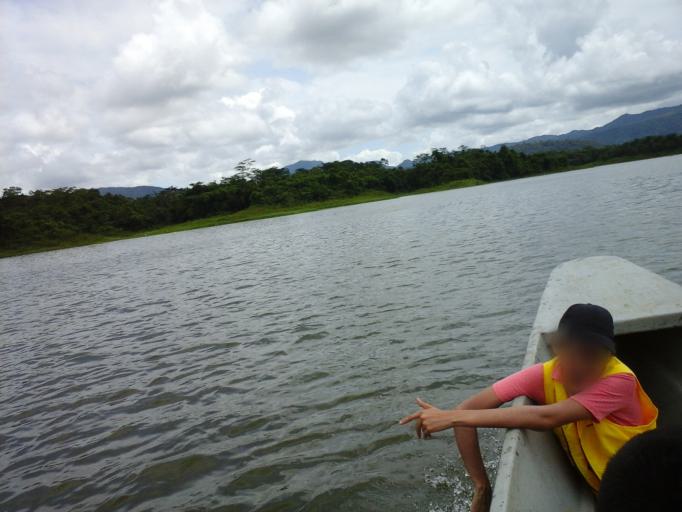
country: CO
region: Bolivar
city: San Cristobal
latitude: 9.8713
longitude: -75.2918
